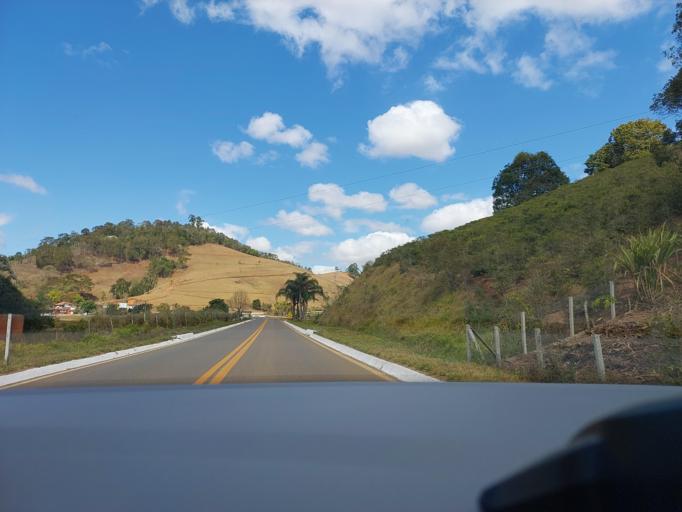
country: BR
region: Minas Gerais
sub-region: Mirai
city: Mirai
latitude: -21.0051
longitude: -42.5533
